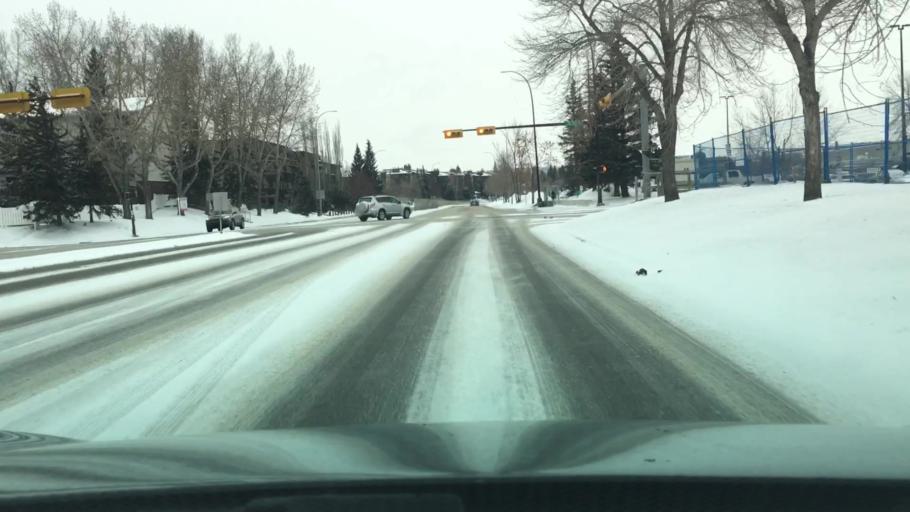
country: CA
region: Alberta
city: Calgary
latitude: 51.0827
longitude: -114.1581
